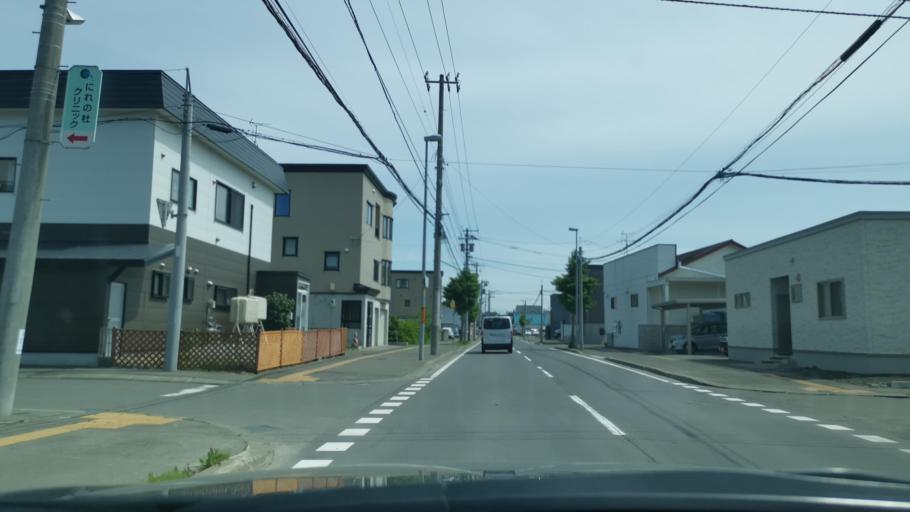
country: JP
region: Hokkaido
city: Sapporo
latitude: 43.0658
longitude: 141.3906
